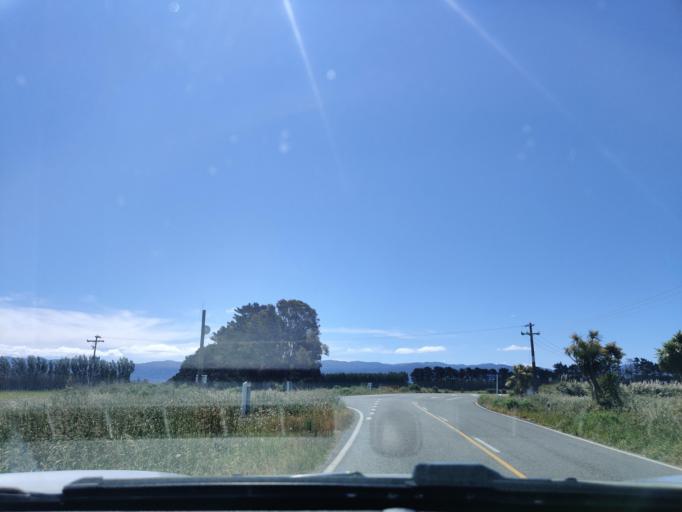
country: NZ
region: Wellington
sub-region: Upper Hutt City
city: Upper Hutt
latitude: -41.2821
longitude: 175.2659
